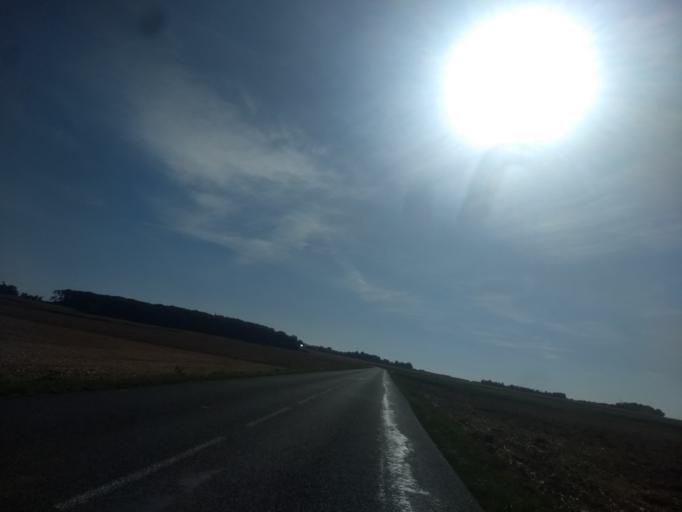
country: FR
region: Nord-Pas-de-Calais
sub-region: Departement du Pas-de-Calais
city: Roeux
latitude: 50.2825
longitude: 2.8997
